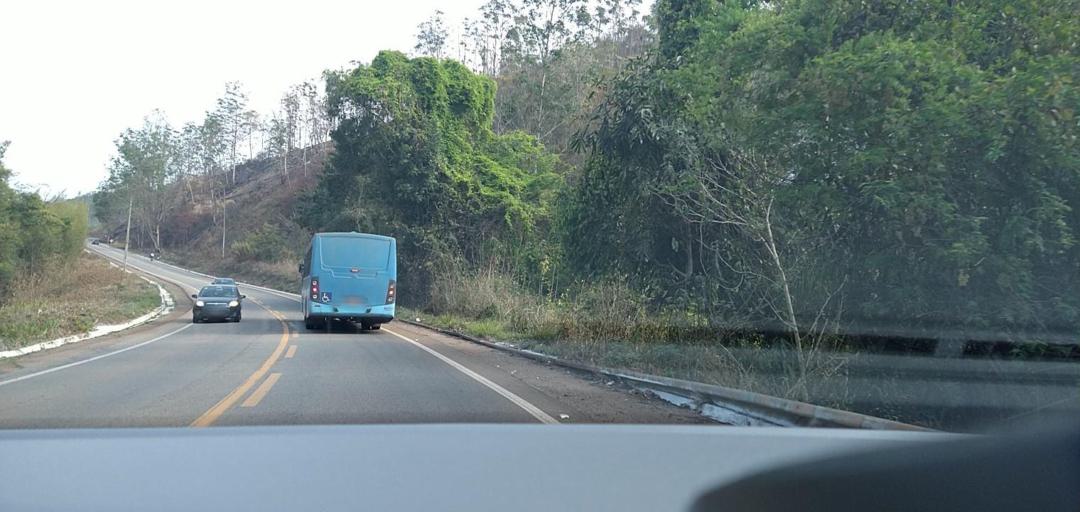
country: BR
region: Minas Gerais
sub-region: Rio Piracicaba
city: Rio Piracicaba
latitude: -19.8710
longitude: -43.1228
